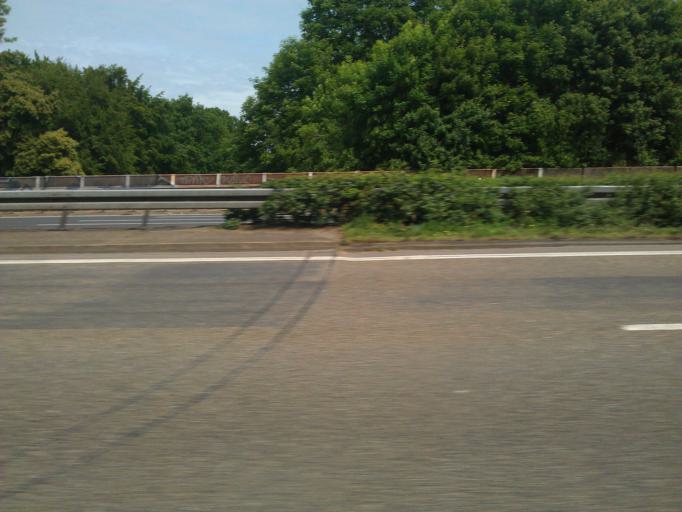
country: DE
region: North Rhine-Westphalia
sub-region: Regierungsbezirk Koln
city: Neustadt/Sued
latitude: 50.8983
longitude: 6.9094
